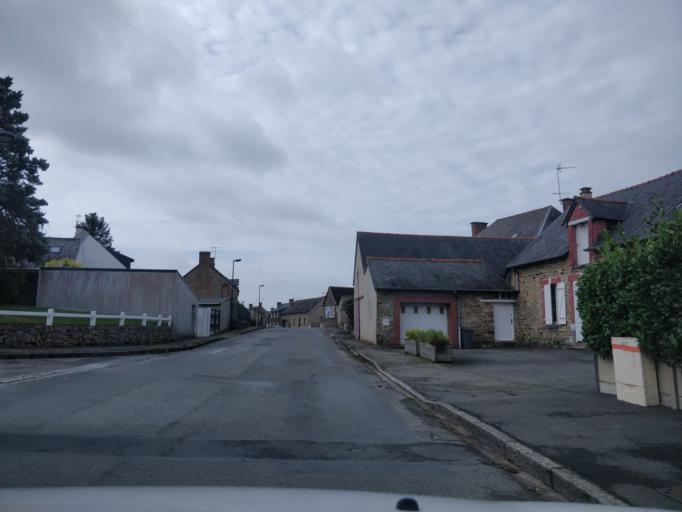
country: FR
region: Brittany
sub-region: Departement d'Ille-et-Vilaine
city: Servon-sur-Vilaine
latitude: 48.1230
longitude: -1.4594
